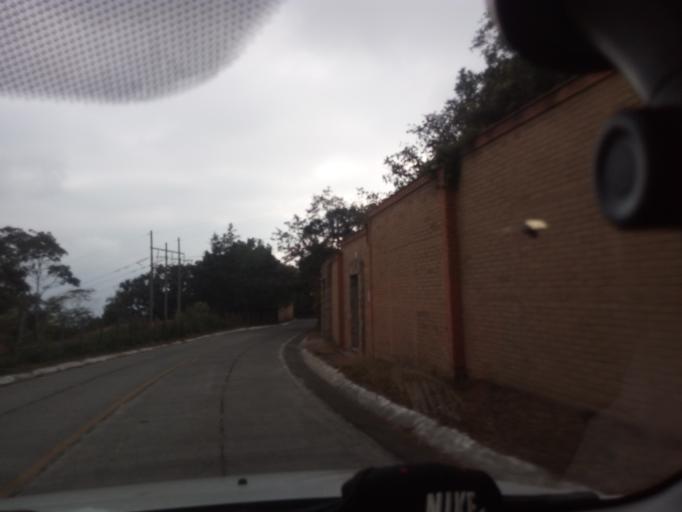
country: GT
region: Sacatepequez
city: Antigua Guatemala
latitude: 14.5708
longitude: -90.7183
